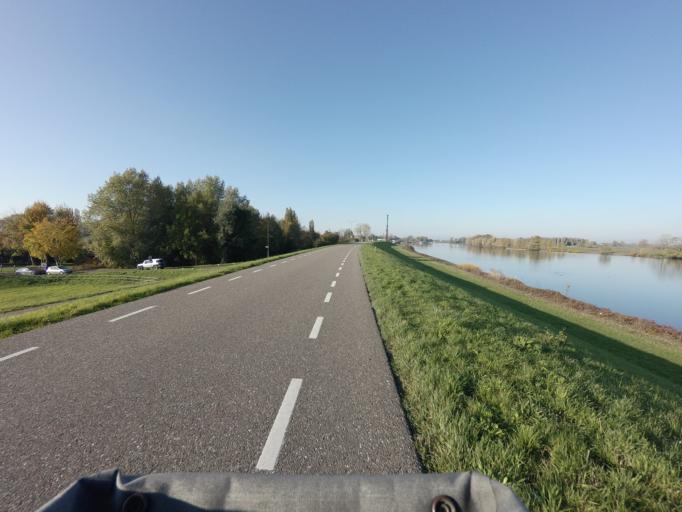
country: NL
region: North Brabant
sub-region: Gemeente Woudrichem
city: Woudrichem
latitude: 51.8074
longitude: 5.0138
